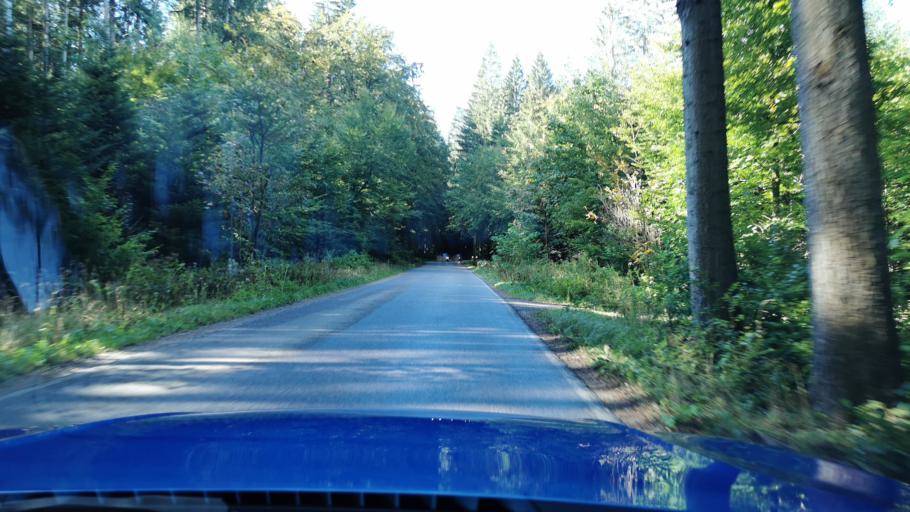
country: DE
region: Bavaria
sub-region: Upper Bavaria
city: Warngau
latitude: 47.8129
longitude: 11.6910
